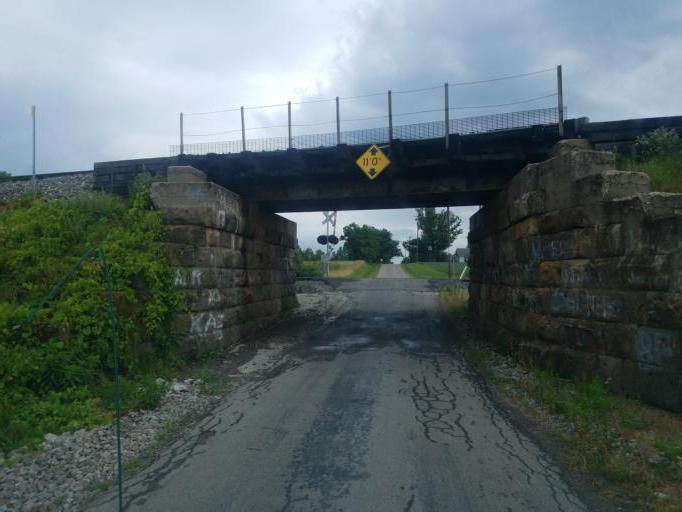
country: US
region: Ohio
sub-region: Defiance County
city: Hicksville
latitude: 41.3040
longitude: -84.8038
